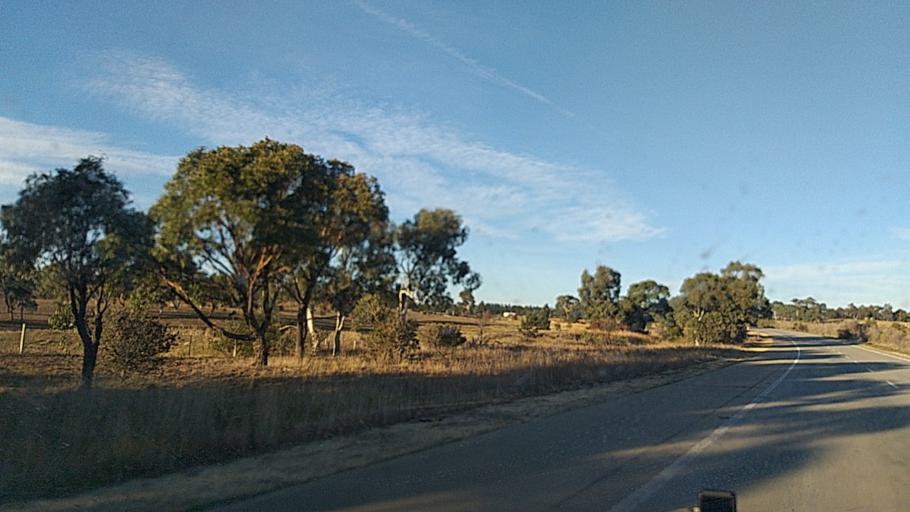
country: AU
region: New South Wales
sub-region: Yass Valley
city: Gundaroo
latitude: -35.1201
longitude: 149.3475
